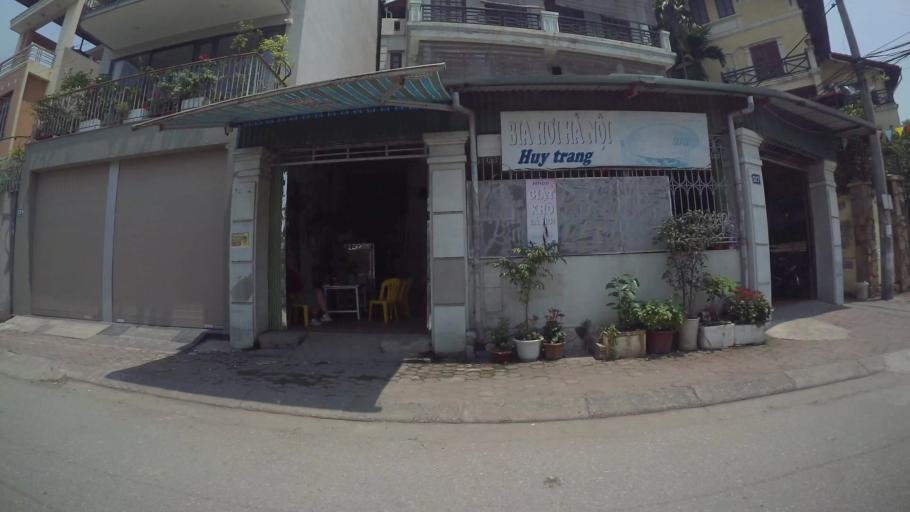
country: VN
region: Ha Noi
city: Hoan Kiem
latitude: 21.0351
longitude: 105.8761
